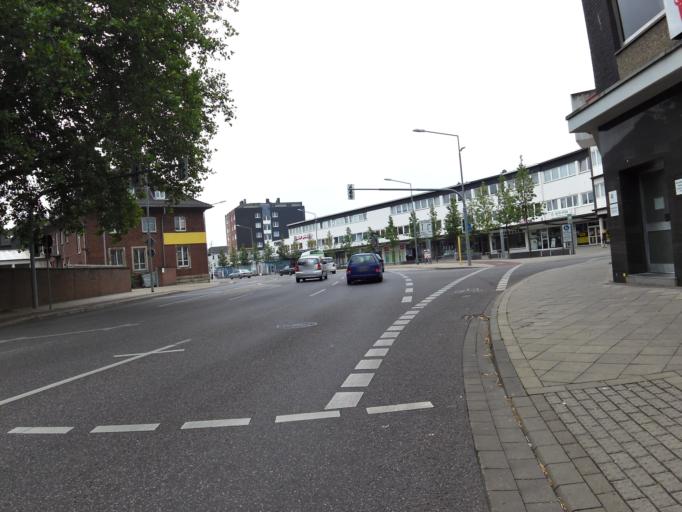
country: DE
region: North Rhine-Westphalia
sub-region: Regierungsbezirk Koln
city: Alsdorf
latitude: 50.8750
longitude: 6.1593
